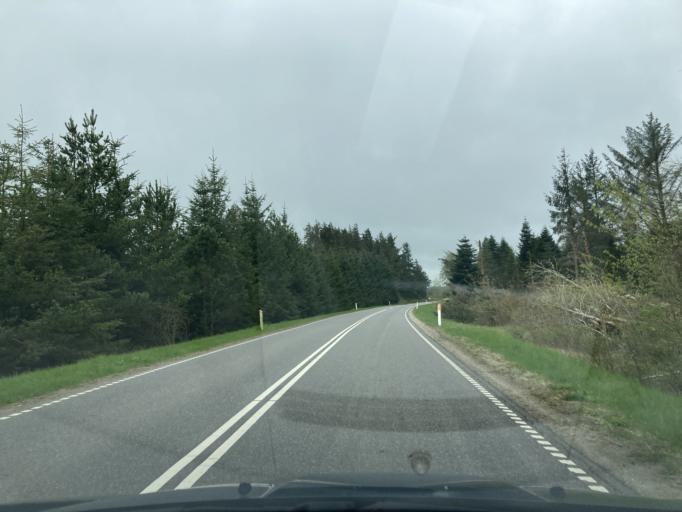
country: DK
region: North Denmark
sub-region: Thisted Kommune
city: Hurup
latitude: 56.8683
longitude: 8.3835
